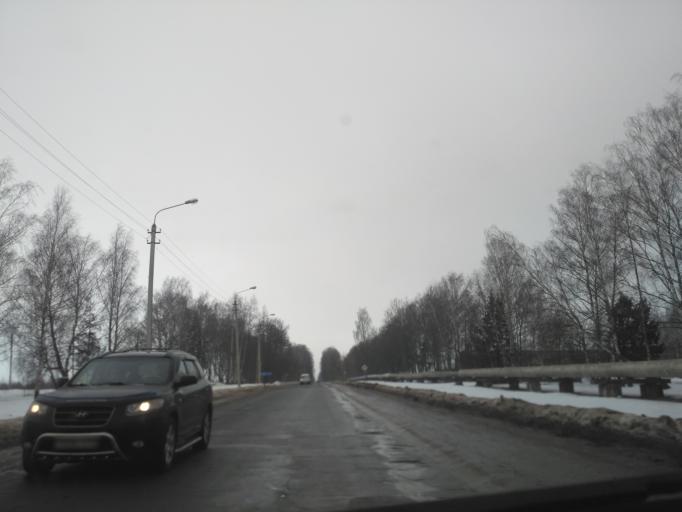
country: BY
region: Minsk
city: Horad Zhodzina
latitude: 54.0911
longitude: 28.3286
